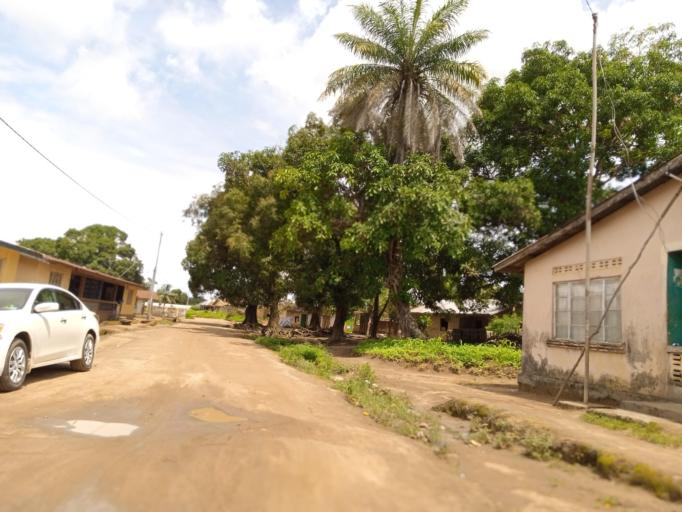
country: SL
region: Northern Province
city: Masoyila
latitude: 8.6095
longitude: -13.1888
